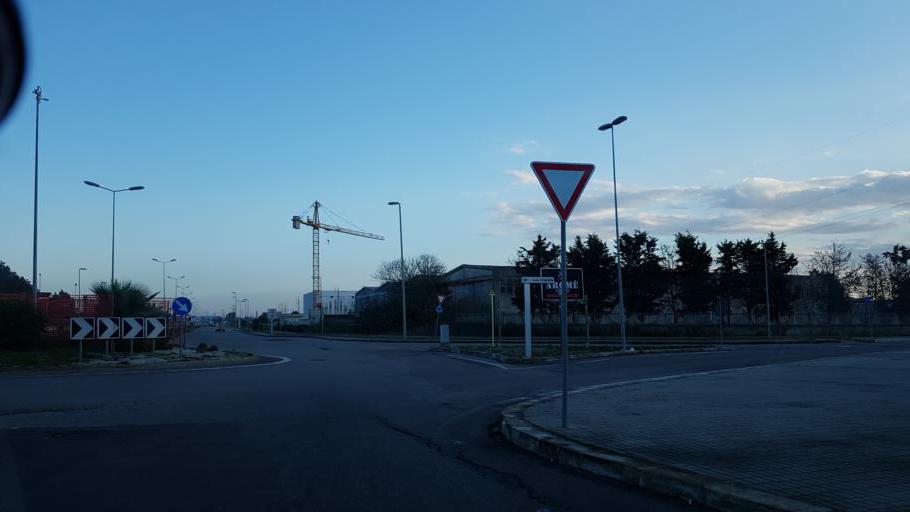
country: IT
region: Apulia
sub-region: Provincia di Lecce
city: Surbo
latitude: 40.3775
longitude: 18.1300
